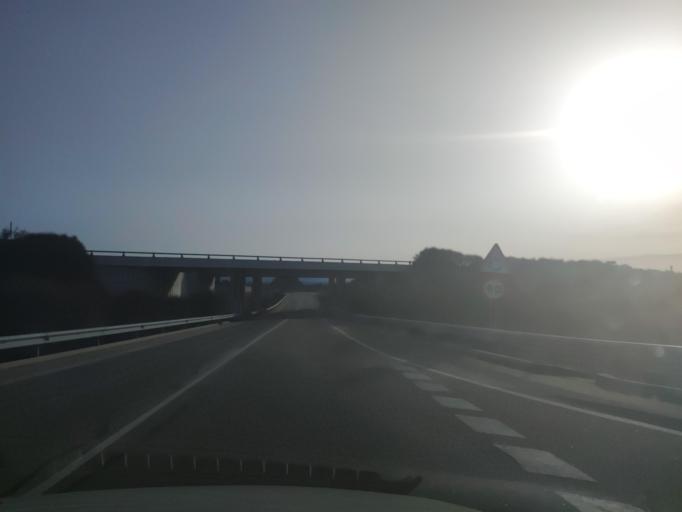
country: ES
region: Castille and Leon
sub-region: Provincia de Salamanca
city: Carpio de Azaba
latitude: 40.5937
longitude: -6.6480
